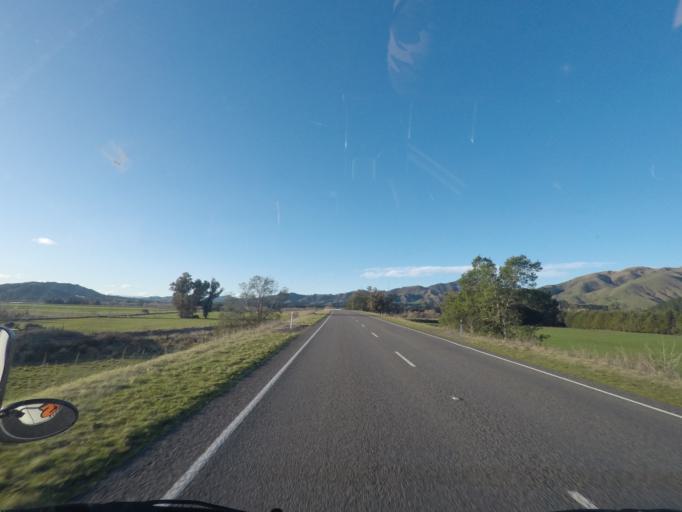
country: NZ
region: Canterbury
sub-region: Kaikoura District
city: Kaikoura
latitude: -42.7065
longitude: 173.2970
